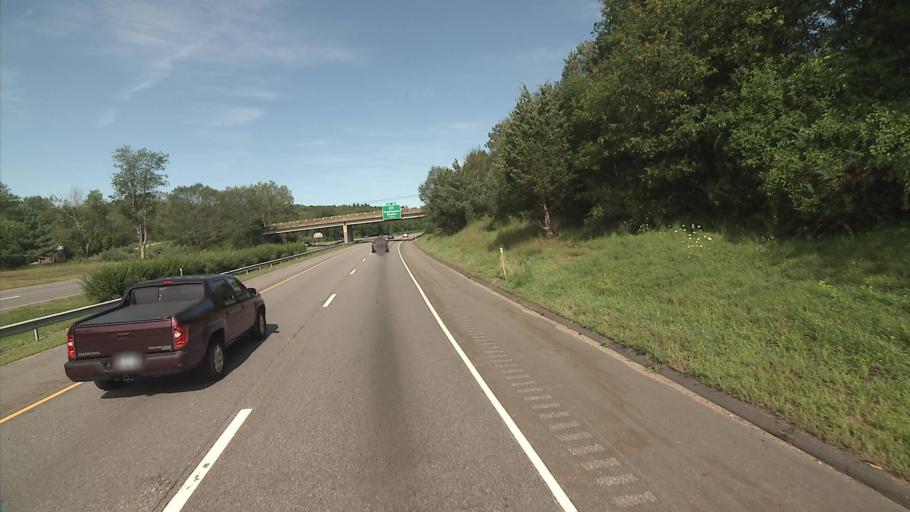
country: US
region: Connecticut
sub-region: New London County
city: Colchester
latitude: 41.5836
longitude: -72.3768
